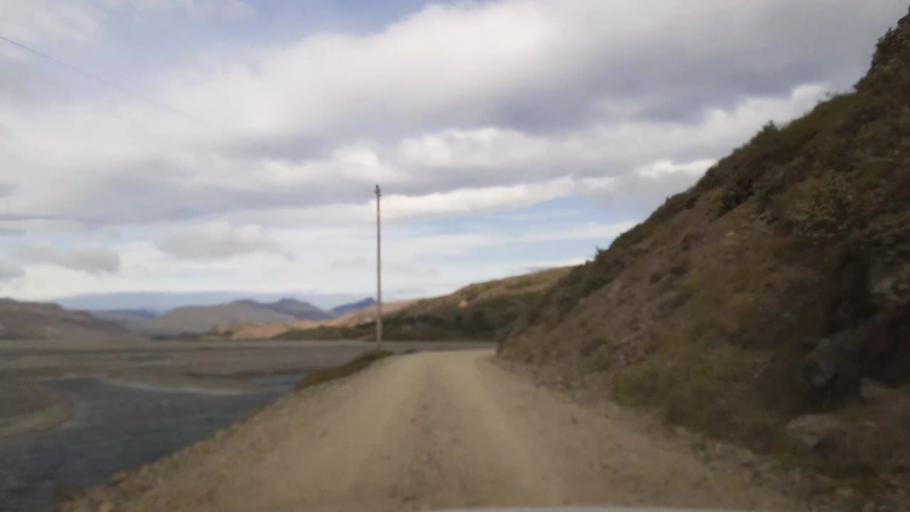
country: IS
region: East
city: Hoefn
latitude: 64.4312
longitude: -14.8901
